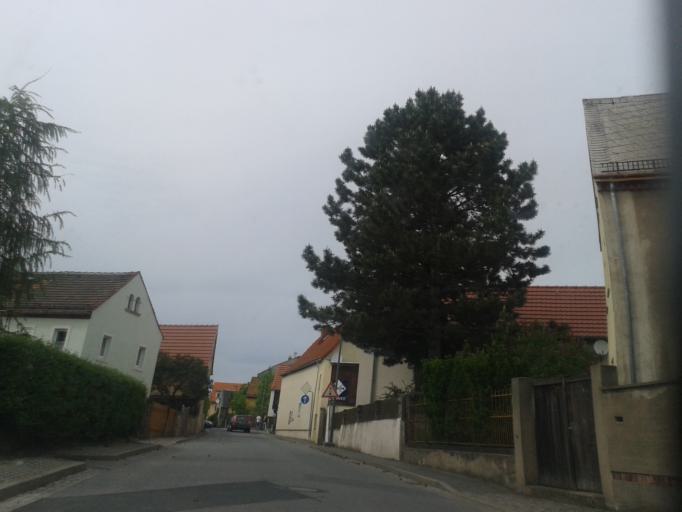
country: DE
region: Saxony
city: Radebeul
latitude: 51.0963
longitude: 13.6767
